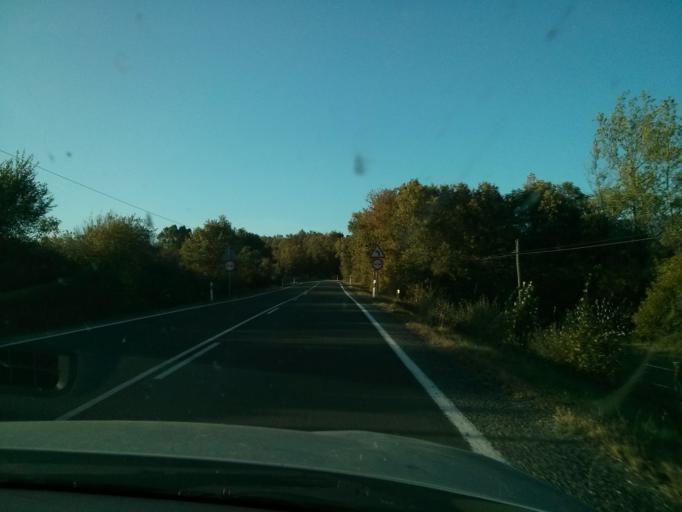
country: ES
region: Castille and Leon
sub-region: Provincia de Burgos
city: Espinosa de los Monteros
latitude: 43.0681
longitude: -3.5105
